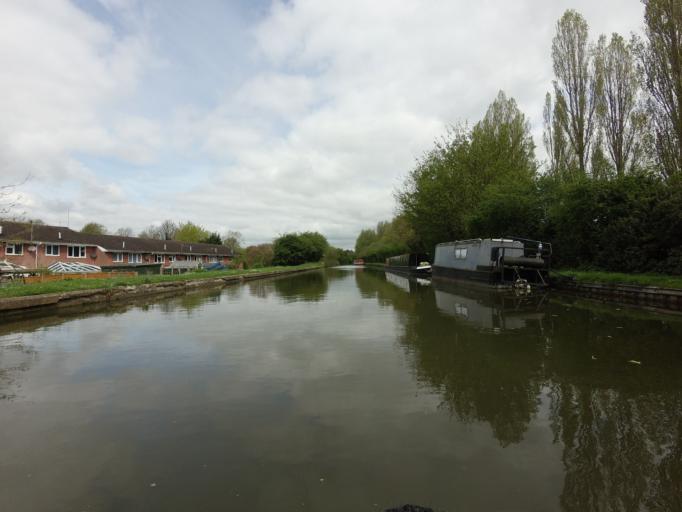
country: GB
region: England
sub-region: Milton Keynes
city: Water Eaton
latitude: 51.9894
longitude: -0.7168
